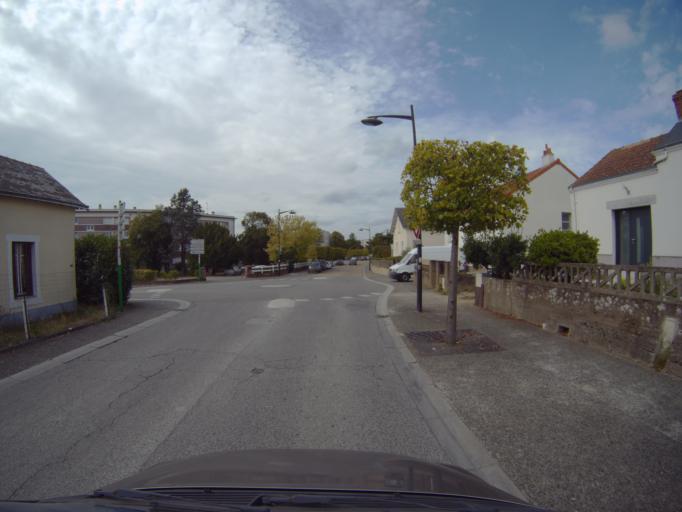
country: FR
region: Pays de la Loire
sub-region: Departement de la Loire-Atlantique
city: Saint-Herblain
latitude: 47.2102
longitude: -1.6465
